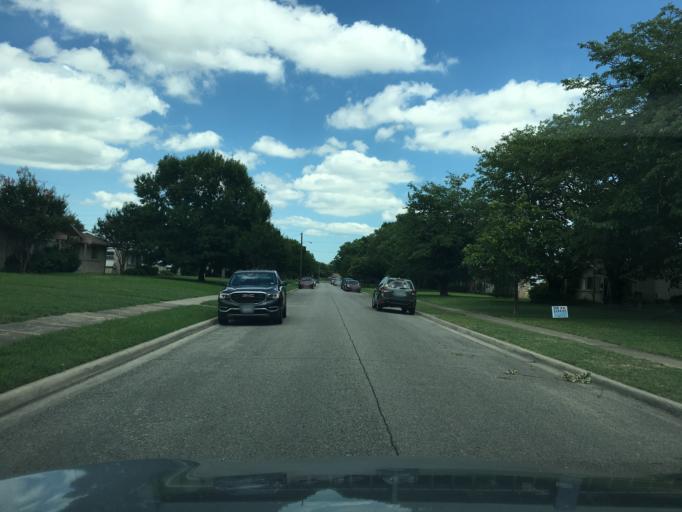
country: US
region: Texas
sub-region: Dallas County
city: Richardson
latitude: 32.9501
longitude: -96.7080
